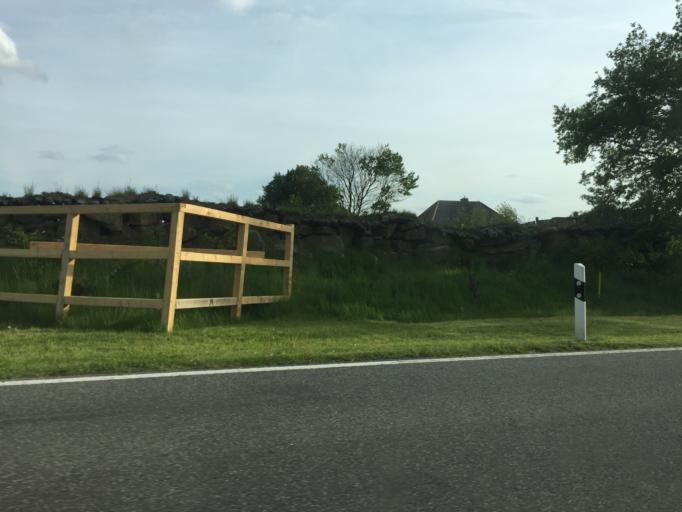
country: DE
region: Saxony
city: Stadt Wehlen
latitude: 50.9877
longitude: 14.0538
